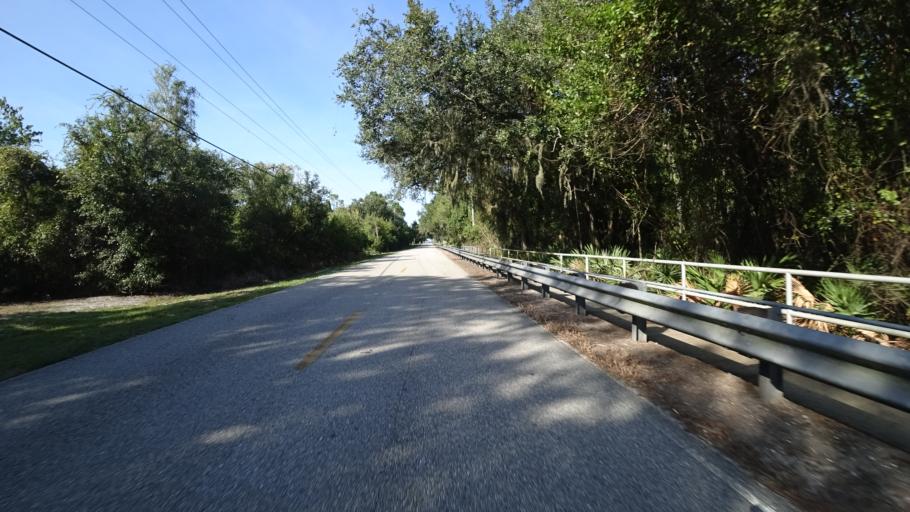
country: US
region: Florida
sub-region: Sarasota County
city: Desoto Lakes
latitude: 27.4346
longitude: -82.4810
